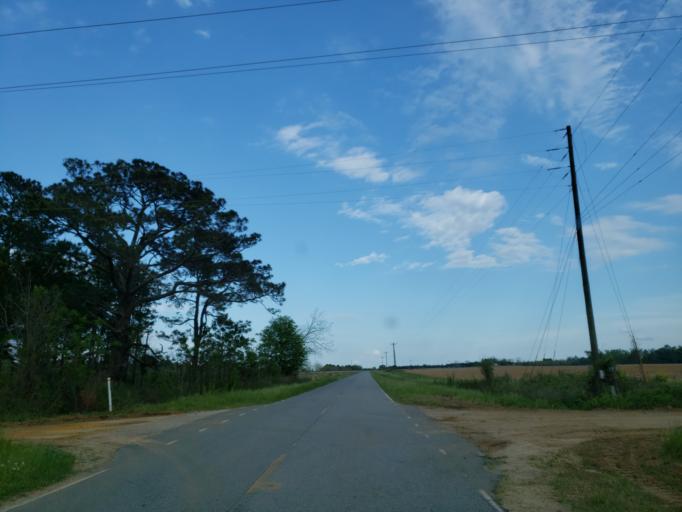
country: US
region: Georgia
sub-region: Dooly County
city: Vienna
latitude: 32.1236
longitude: -83.7046
